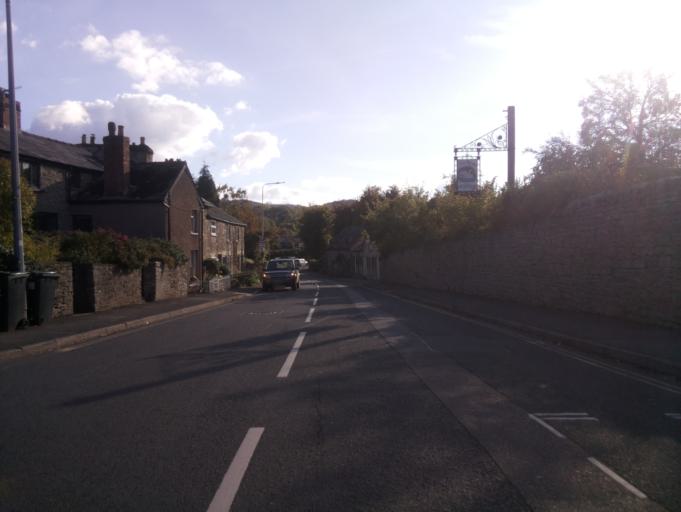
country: GB
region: Wales
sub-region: Sir Powys
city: Hay
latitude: 52.0722
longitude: -3.1291
